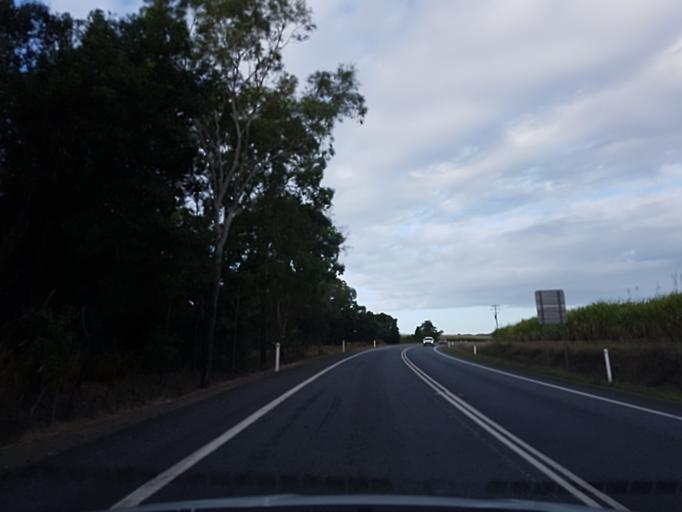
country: AU
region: Queensland
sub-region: Cairns
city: Port Douglas
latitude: -16.5532
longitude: 145.4828
